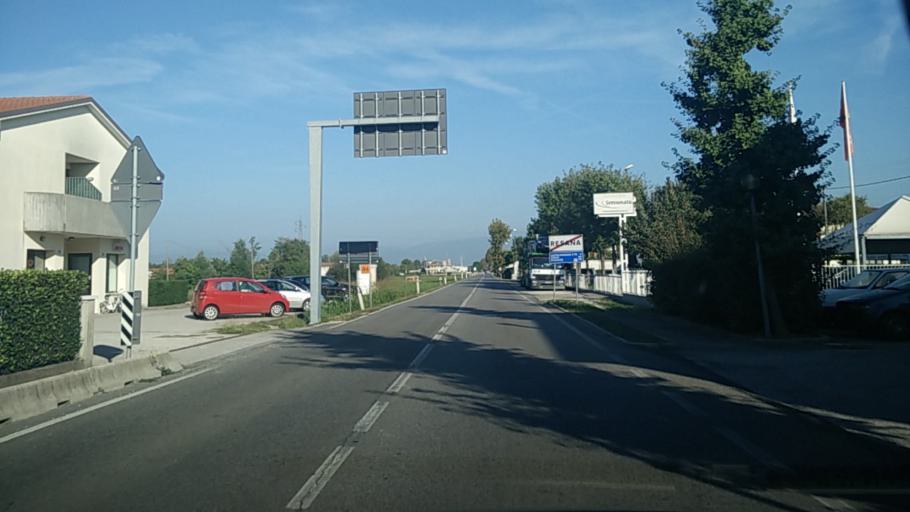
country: IT
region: Veneto
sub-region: Provincia di Treviso
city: Resana
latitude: 45.6410
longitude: 11.9517
